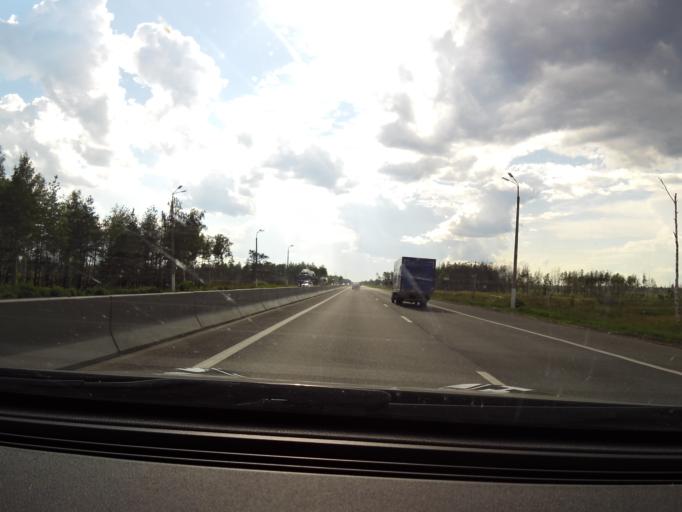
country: RU
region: Nizjnij Novgorod
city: Dzerzhinsk
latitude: 56.3011
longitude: 43.5418
